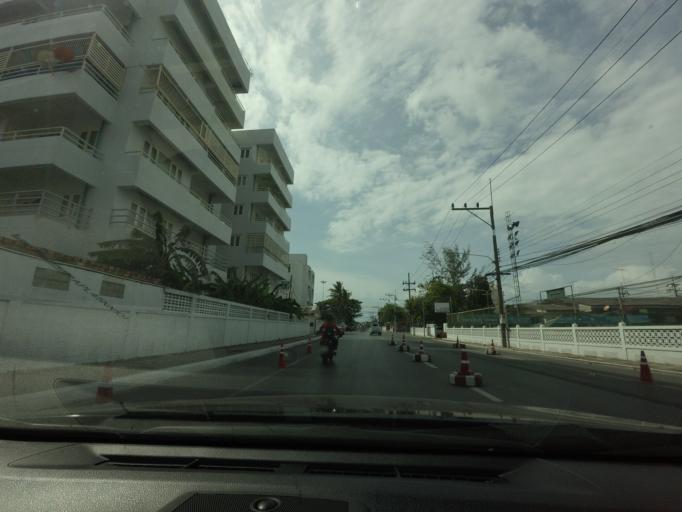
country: TH
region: Pattani
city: Pattani
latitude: 6.8709
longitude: 101.2500
